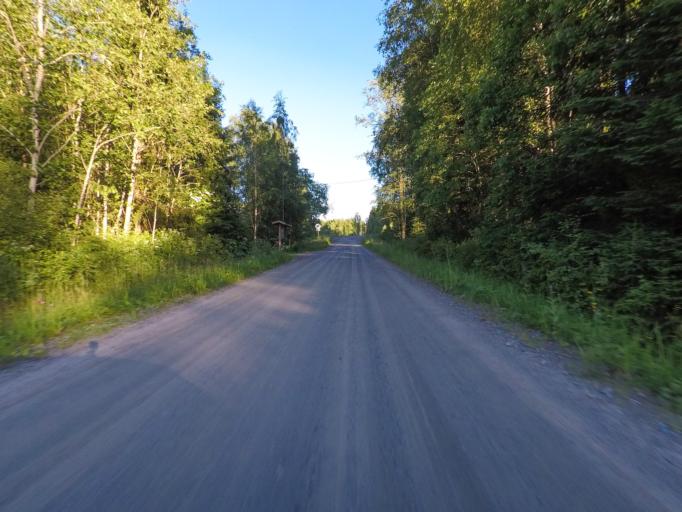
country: FI
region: Northern Savo
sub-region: Kuopio
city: Maaninka
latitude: 62.8796
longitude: 27.2945
